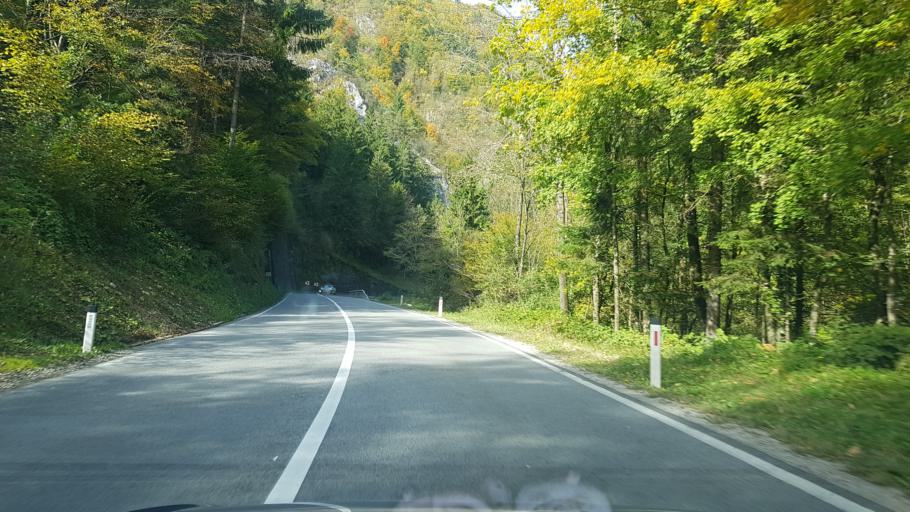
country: SI
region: Velenje
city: Velenje
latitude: 46.4124
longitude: 15.1767
